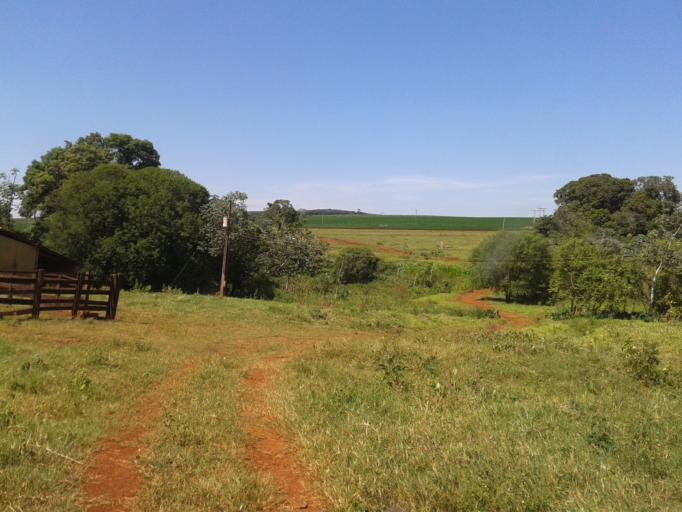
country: BR
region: Minas Gerais
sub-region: Centralina
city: Centralina
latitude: -18.6388
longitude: -49.2950
